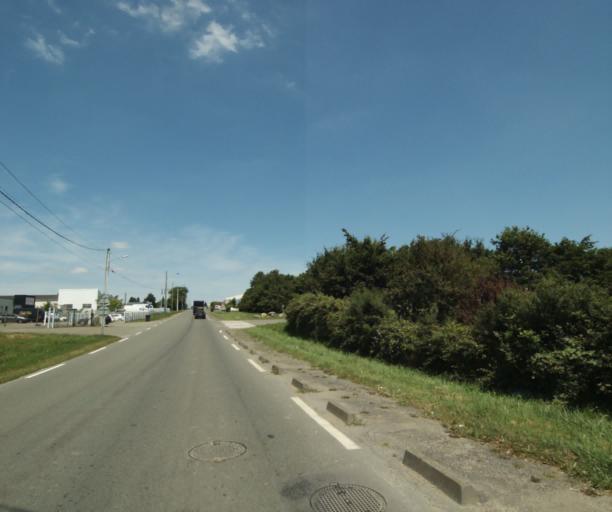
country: FR
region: Pays de la Loire
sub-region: Departement de la Mayenne
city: Laval
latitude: 48.0828
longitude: -0.7401
